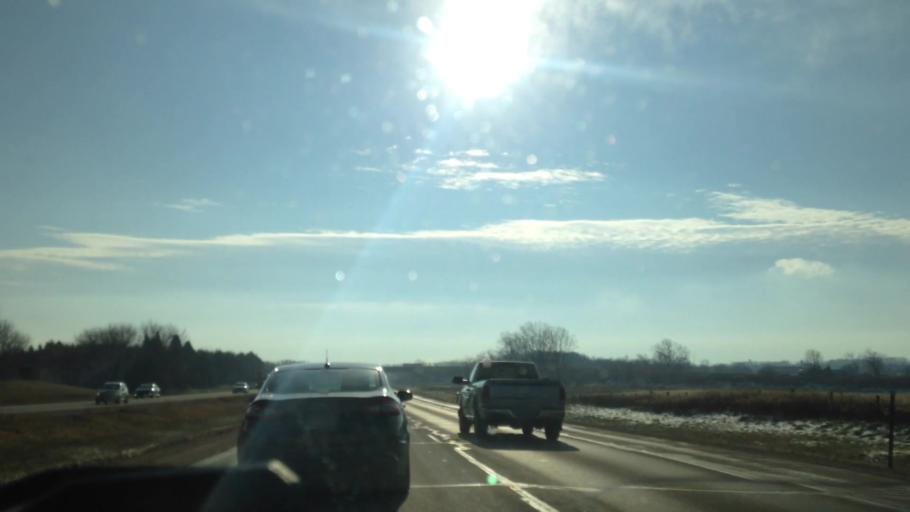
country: US
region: Wisconsin
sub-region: Washington County
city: Slinger
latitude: 43.3134
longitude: -88.2356
